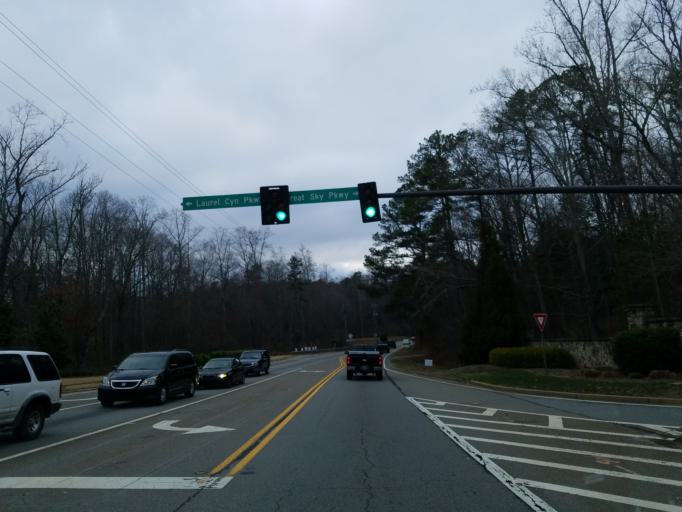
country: US
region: Georgia
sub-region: Cherokee County
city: Canton
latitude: 34.2730
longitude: -84.5039
